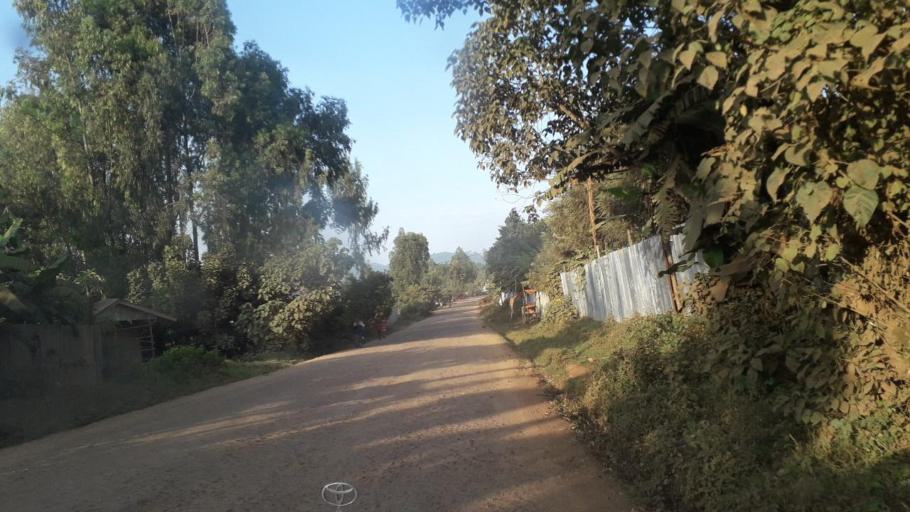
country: ET
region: Oromiya
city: Jima
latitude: 7.6323
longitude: 36.8318
